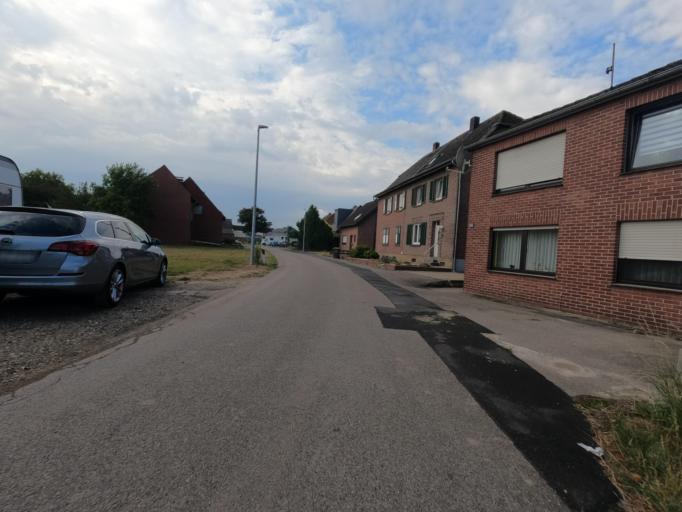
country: DE
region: North Rhine-Westphalia
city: Wegberg
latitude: 51.1104
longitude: 6.2667
